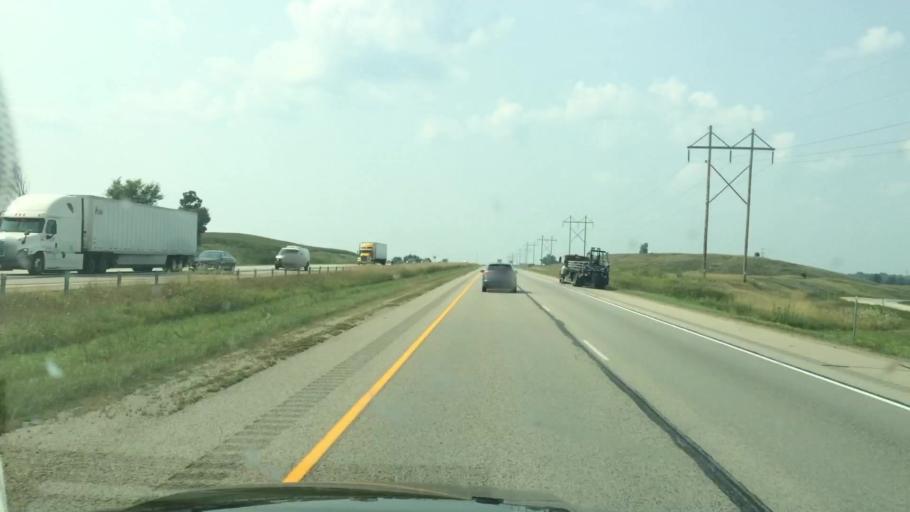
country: US
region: Wisconsin
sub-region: Fond du Lac County
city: North Fond du Lac
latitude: 43.8463
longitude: -88.5645
